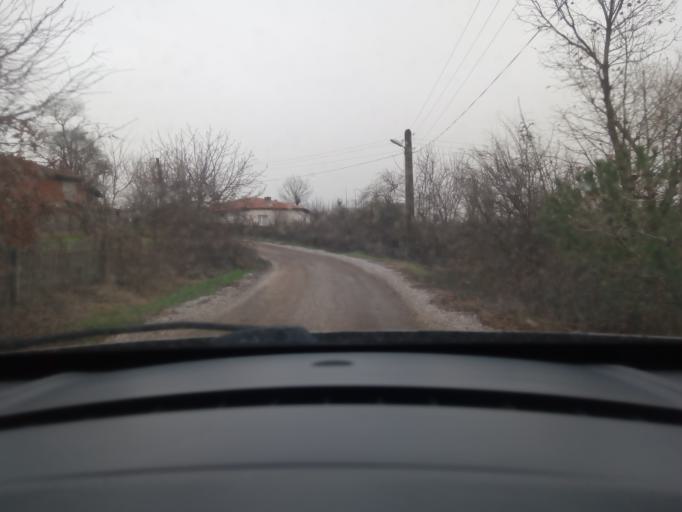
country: TR
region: Balikesir
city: Omerkoy
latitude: 39.8898
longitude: 28.0457
